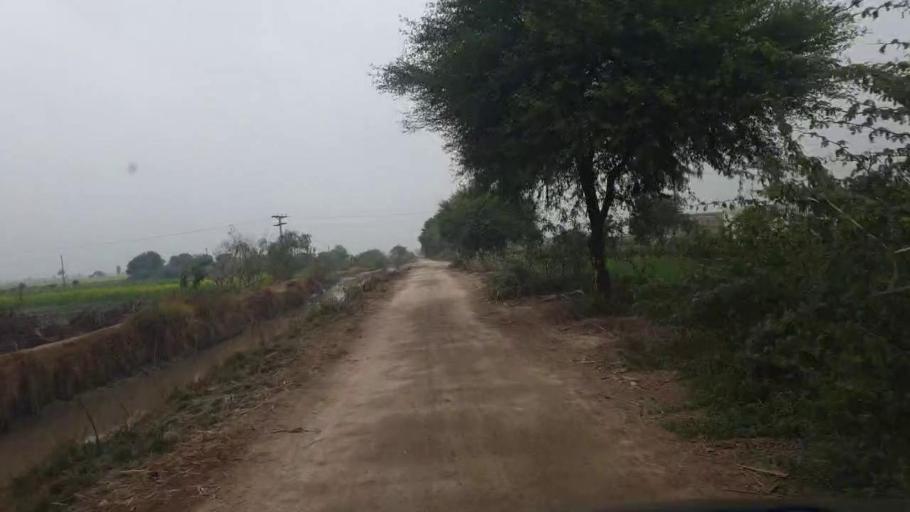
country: PK
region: Sindh
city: Tando Adam
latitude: 25.8506
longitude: 68.6757
